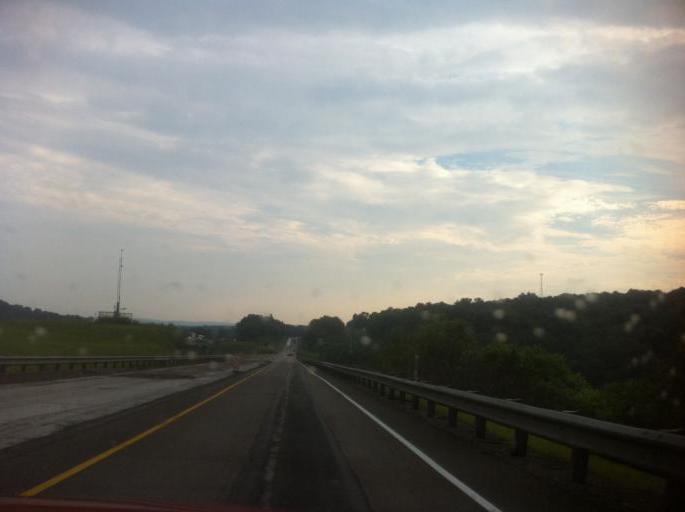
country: US
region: Pennsylvania
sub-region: Clarion County
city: Knox
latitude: 41.1932
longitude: -79.5123
